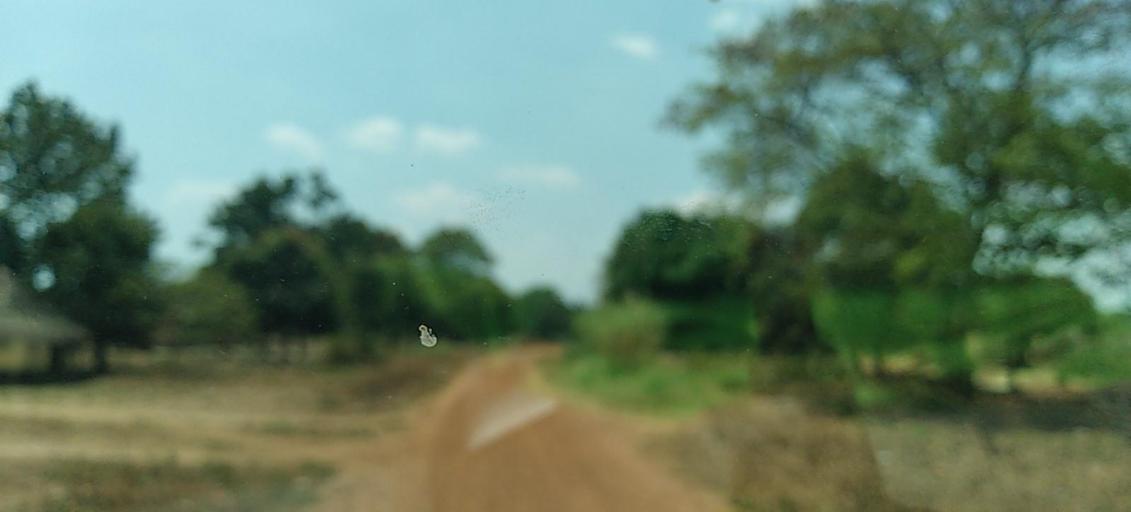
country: CD
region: Katanga
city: Kolwezi
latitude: -11.2959
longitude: 25.2101
